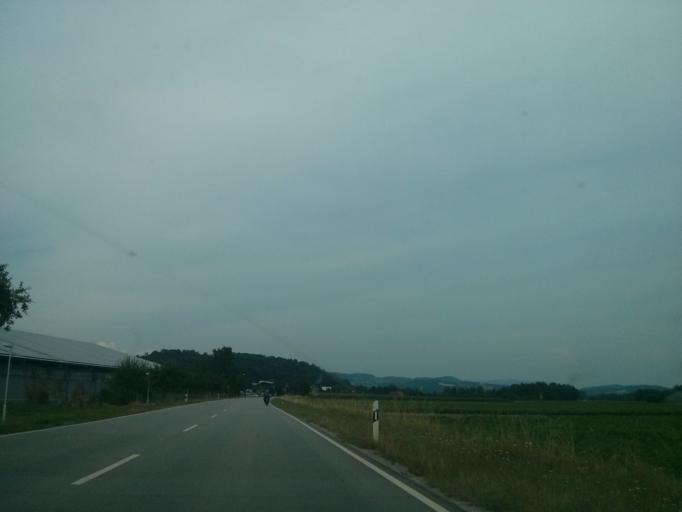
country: DE
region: Bavaria
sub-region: Lower Bavaria
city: Metten
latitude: 48.8202
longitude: 12.8958
